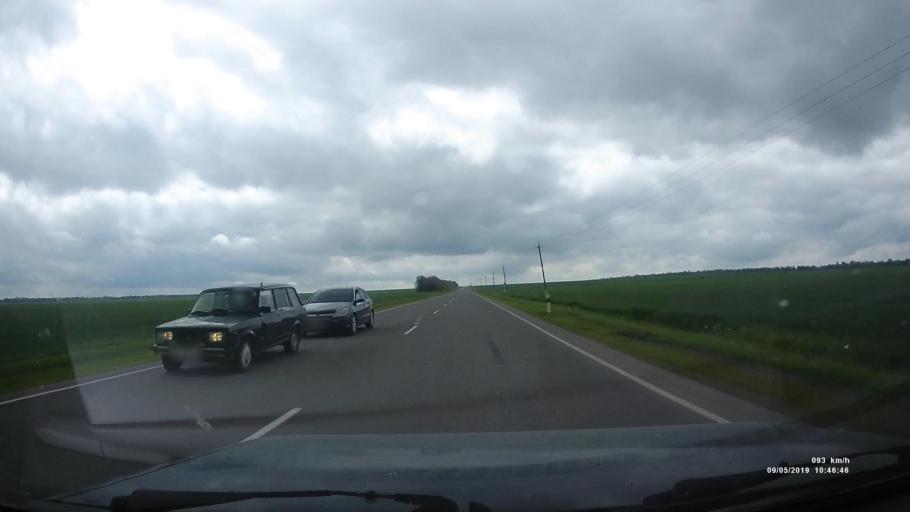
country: RU
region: Rostov
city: Peshkovo
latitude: 46.9801
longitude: 39.3557
